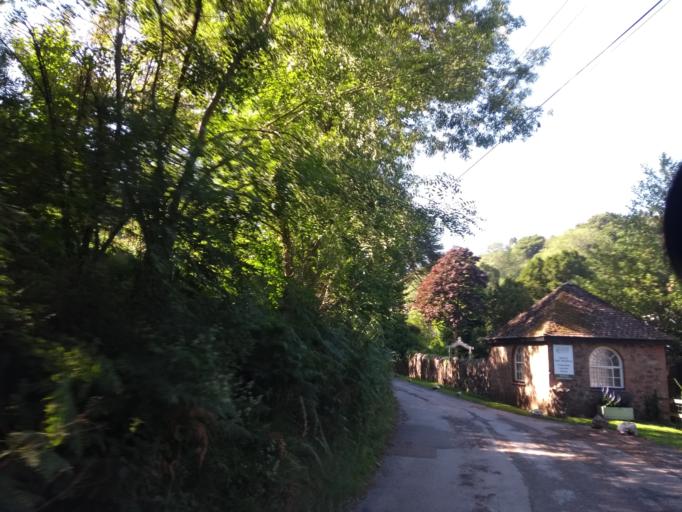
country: GB
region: England
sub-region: Somerset
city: Bishops Lydeard
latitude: 51.1583
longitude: -3.2146
